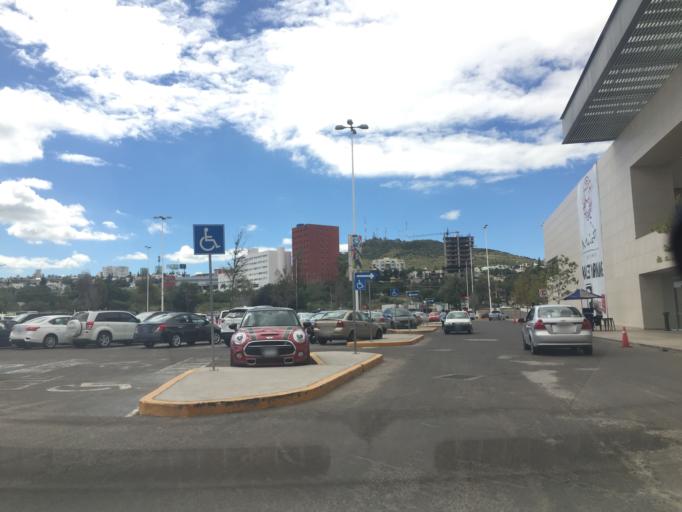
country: MX
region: Guanajuato
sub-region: Leon
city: La Ermita
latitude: 21.1576
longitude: -101.6967
